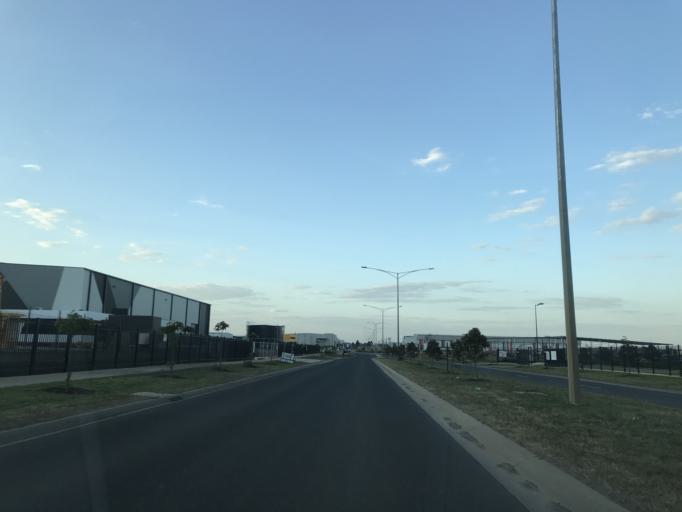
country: AU
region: Victoria
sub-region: Wyndham
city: Truganina
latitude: -37.8334
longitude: 144.7631
